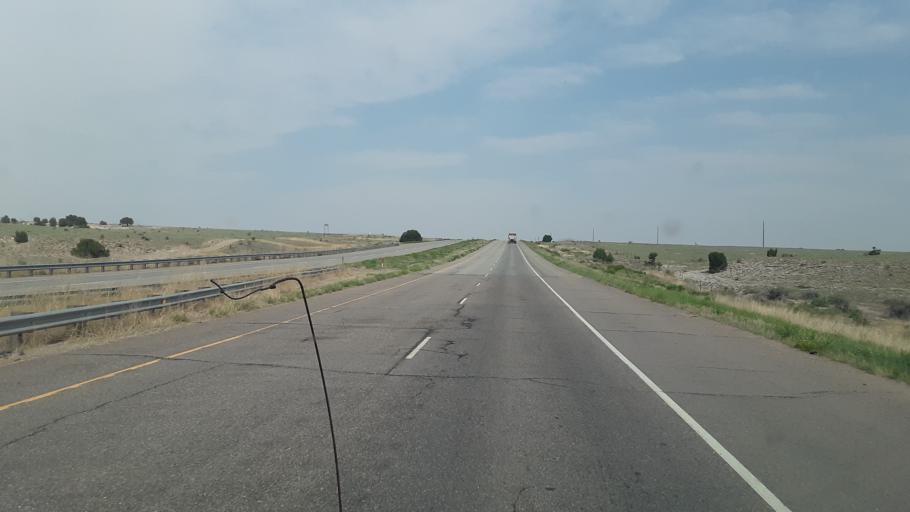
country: US
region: Colorado
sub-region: Pueblo County
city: Pueblo West
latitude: 38.3538
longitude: -104.8337
